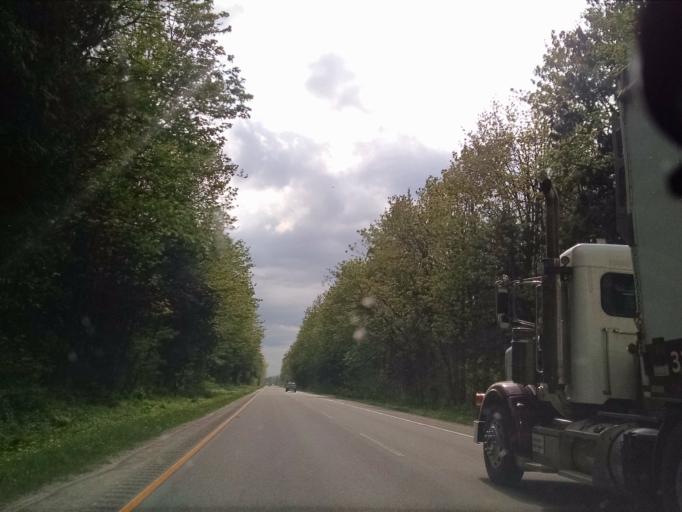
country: CA
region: British Columbia
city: Hope
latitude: 49.3400
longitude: -121.5995
